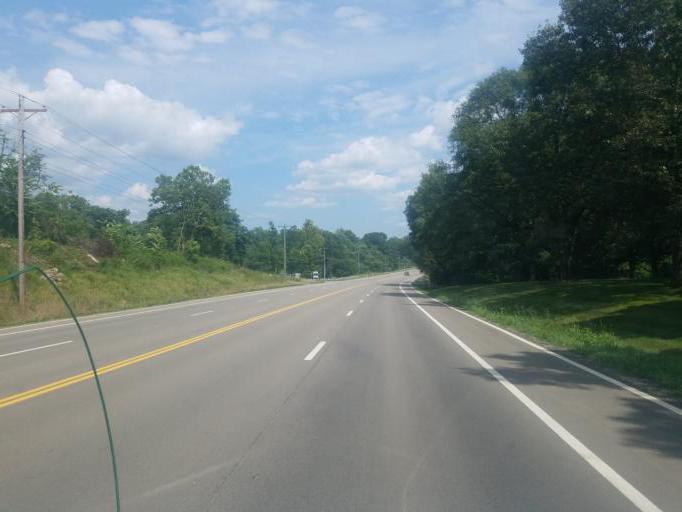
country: US
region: Ohio
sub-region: Muskingum County
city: Zanesville
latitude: 39.9542
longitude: -82.1373
